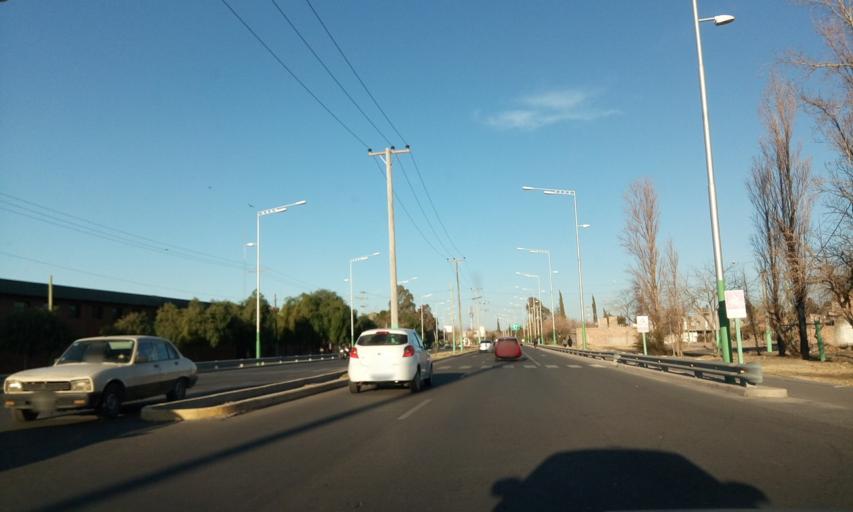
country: AR
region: San Juan
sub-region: Departamento de Rivadavia
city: Rivadavia
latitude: -31.5299
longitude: -68.6005
